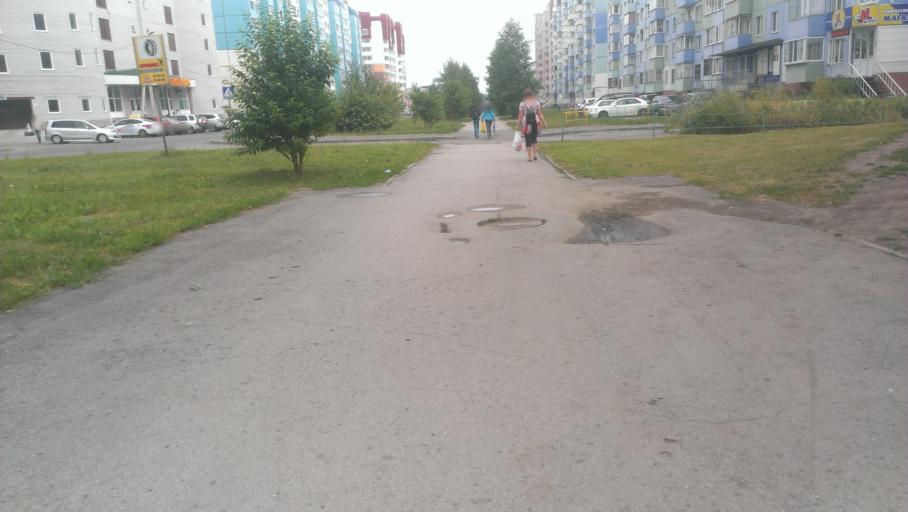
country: RU
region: Altai Krai
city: Novosilikatnyy
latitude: 53.3332
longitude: 83.6848
